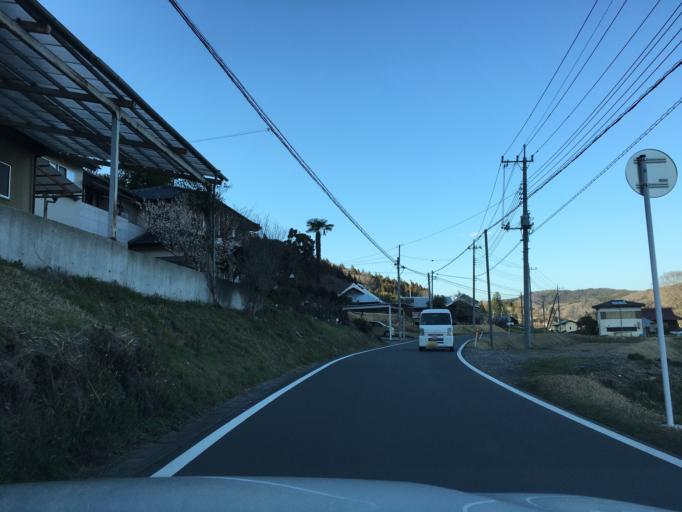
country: JP
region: Tochigi
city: Karasuyama
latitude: 36.7743
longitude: 140.2064
